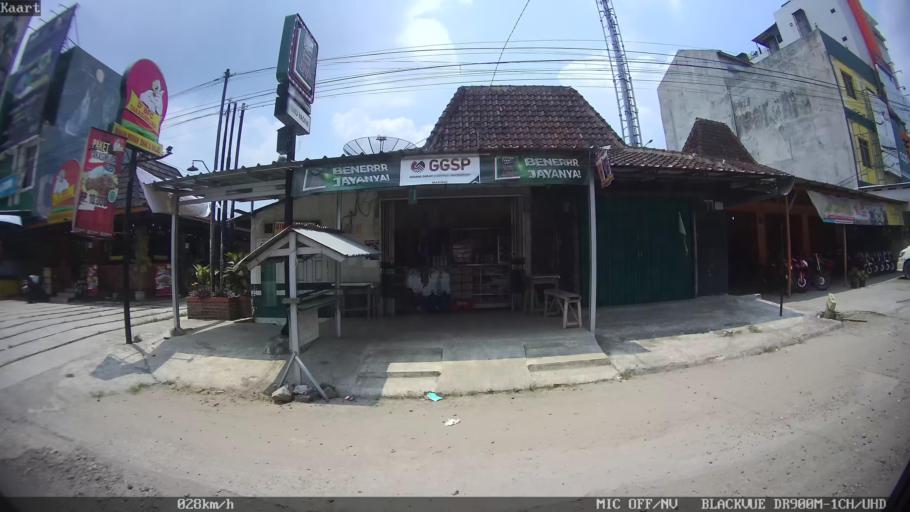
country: ID
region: Lampung
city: Pringsewu
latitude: -5.3568
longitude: 104.9832
